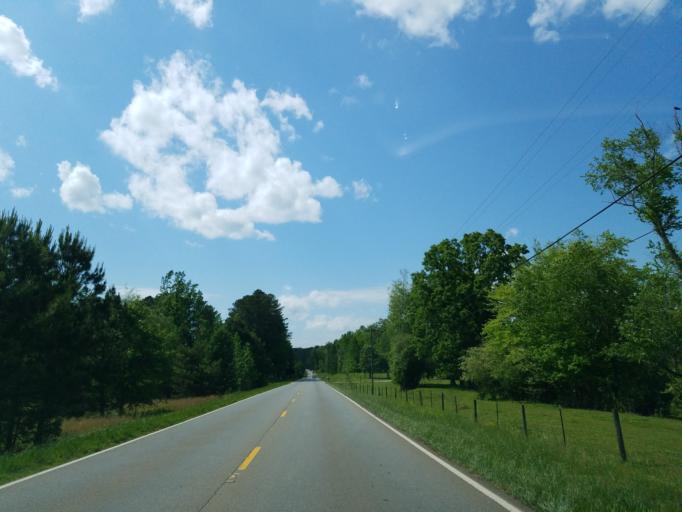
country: US
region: Georgia
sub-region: Cherokee County
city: Ball Ground
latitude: 34.2843
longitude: -84.3019
